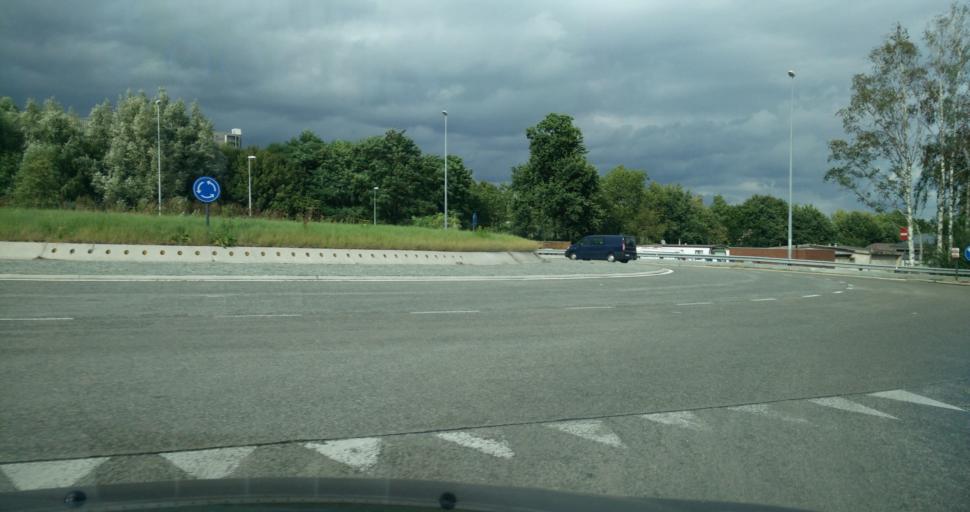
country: BE
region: Flanders
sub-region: Provincie Oost-Vlaanderen
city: Ledeberg
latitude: 51.0233
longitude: 3.7318
